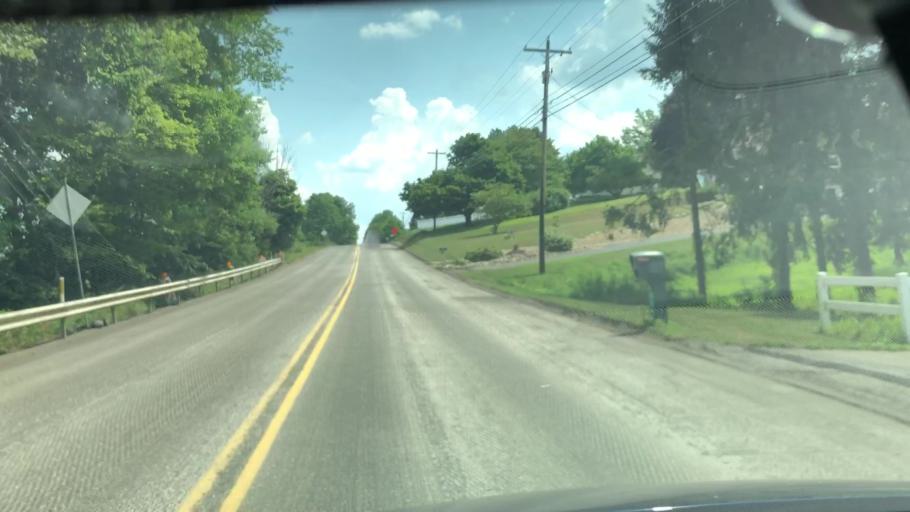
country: US
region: Pennsylvania
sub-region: Butler County
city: Saxonburg
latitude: 40.7901
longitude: -79.8073
